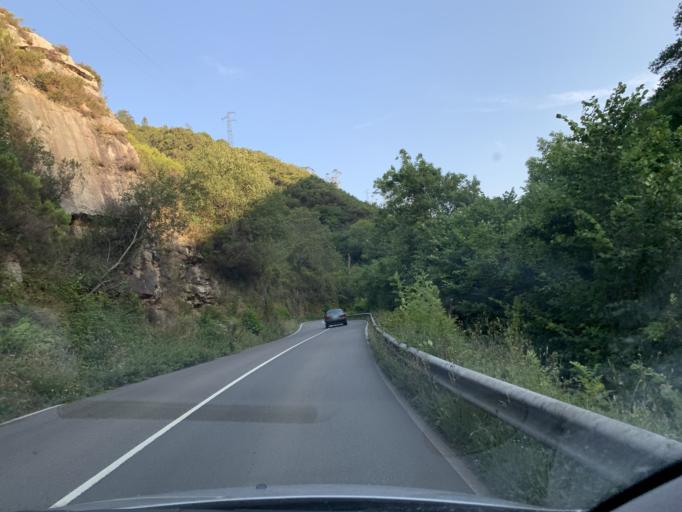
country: ES
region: Asturias
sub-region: Province of Asturias
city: Carrena
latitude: 43.3538
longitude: -4.9147
